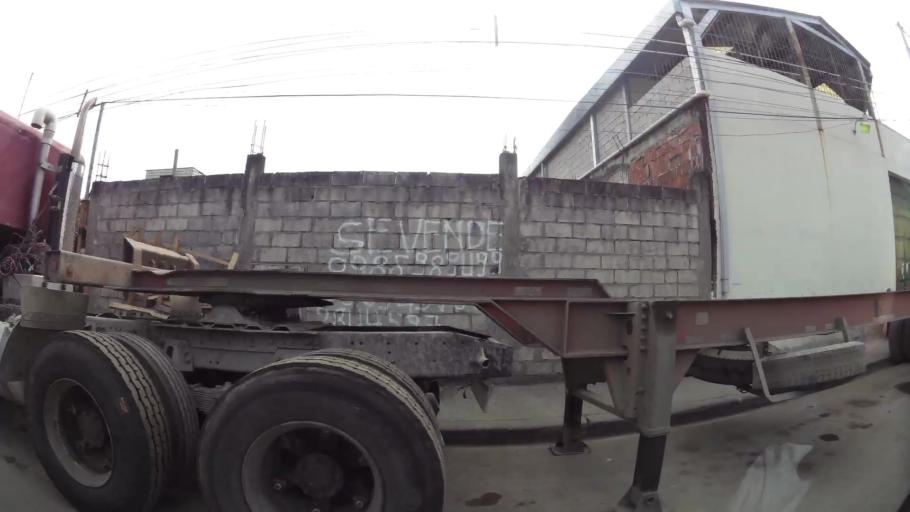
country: EC
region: Guayas
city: Guayaquil
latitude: -2.2602
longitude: -79.8967
